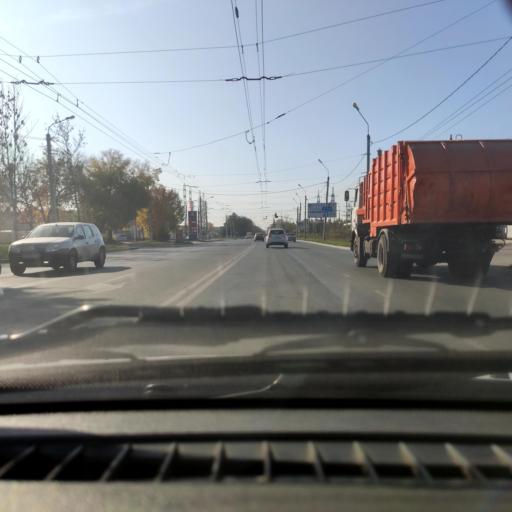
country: RU
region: Samara
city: Tol'yatti
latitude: 53.5348
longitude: 49.4408
